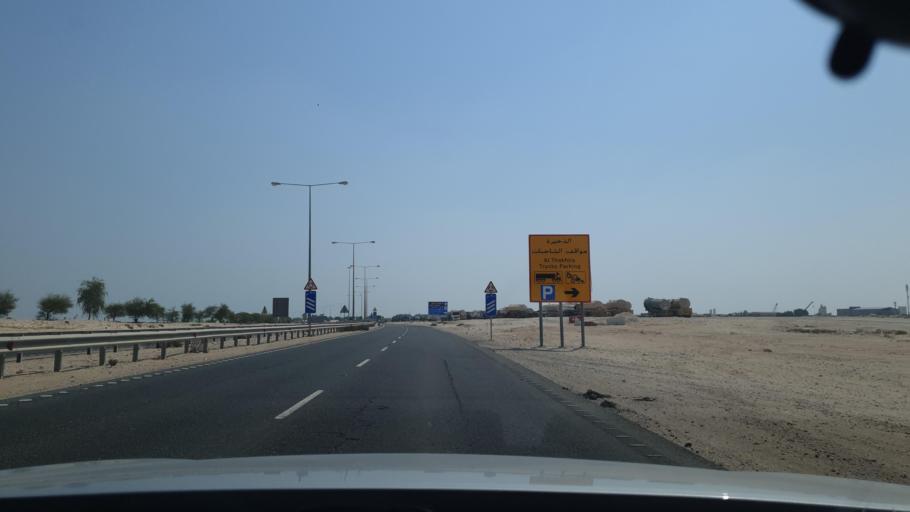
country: QA
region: Al Khawr
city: Al Khawr
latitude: 25.7243
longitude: 51.4975
